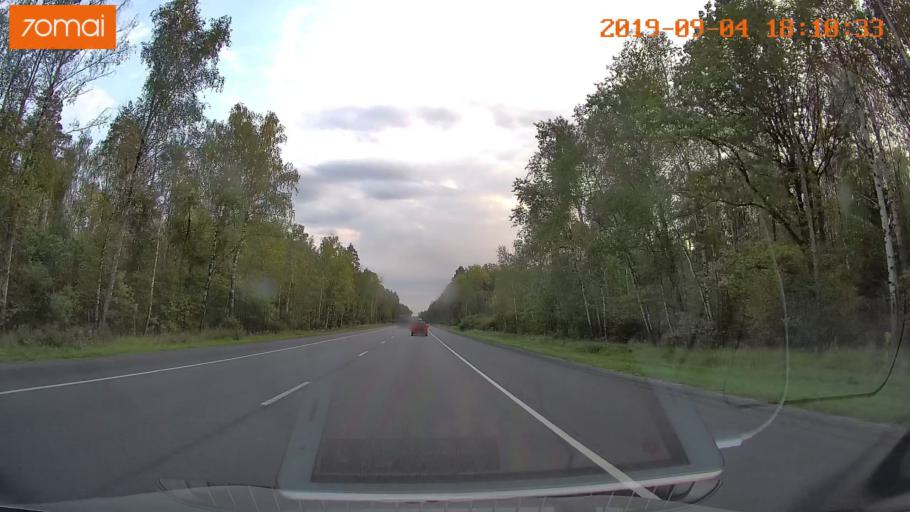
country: RU
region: Moskovskaya
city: Lopatinskiy
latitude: 55.3866
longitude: 38.7641
